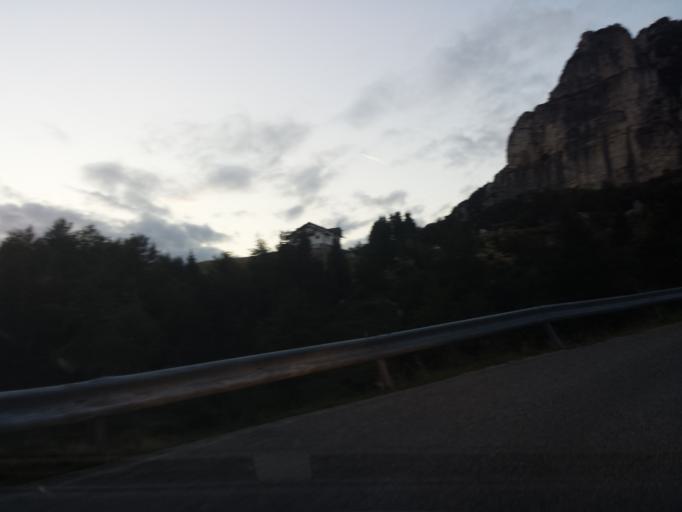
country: IT
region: Veneto
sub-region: Provincia di Vicenza
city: Recoaro Terme
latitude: 45.7270
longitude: 11.1758
